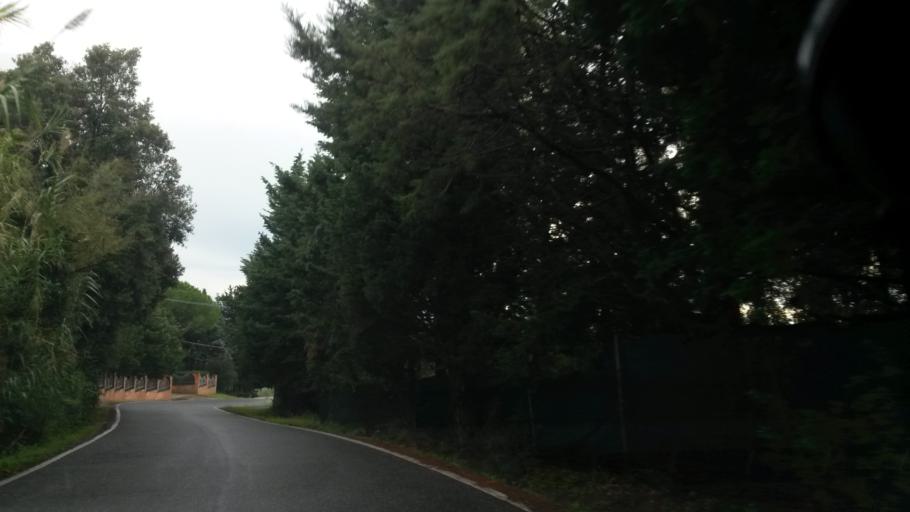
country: IT
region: Tuscany
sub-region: Provincia di Livorno
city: Rosignano Solvay-Castiglioncello
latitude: 43.4080
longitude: 10.4483
